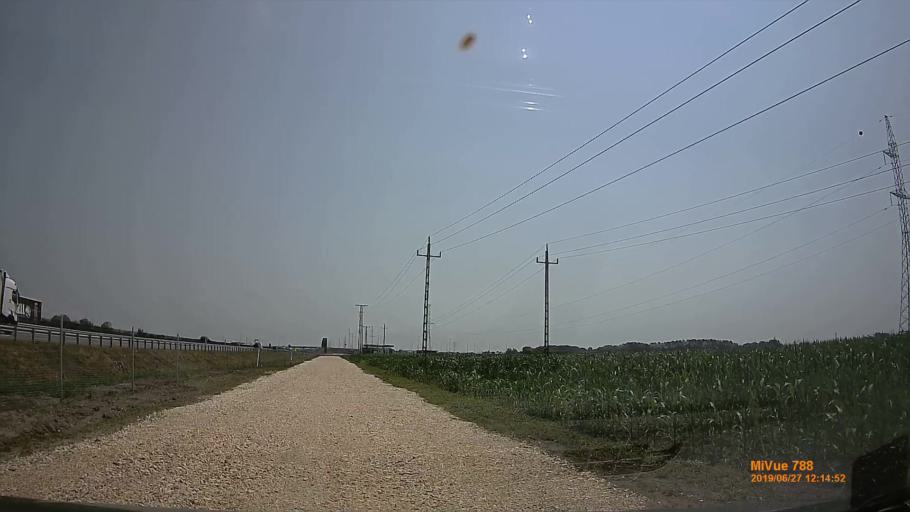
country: HU
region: Pest
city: Cegled
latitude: 47.2049
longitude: 19.7710
